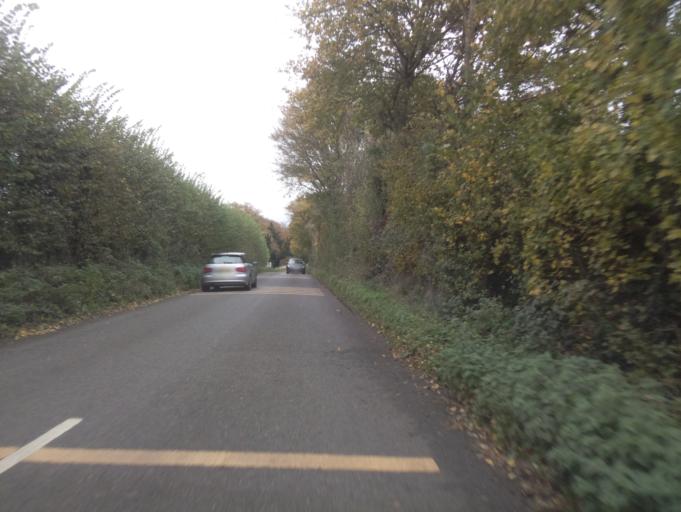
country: GB
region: England
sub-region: Somerset
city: Ilchester
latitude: 51.0167
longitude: -2.6004
